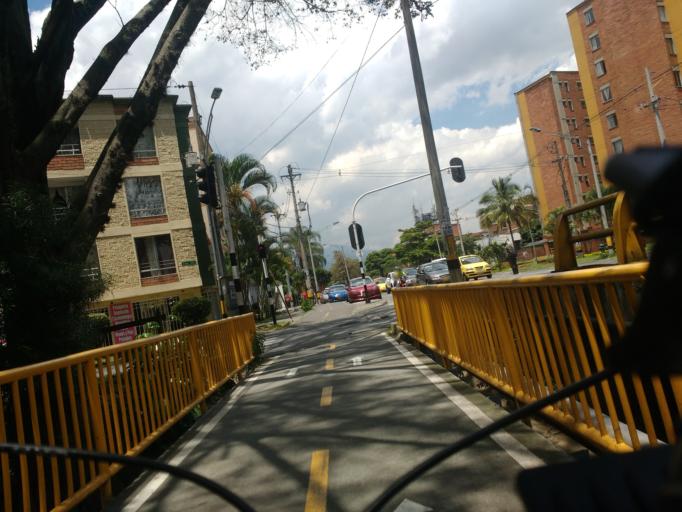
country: CO
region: Antioquia
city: Medellin
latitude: 6.2293
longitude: -75.5913
